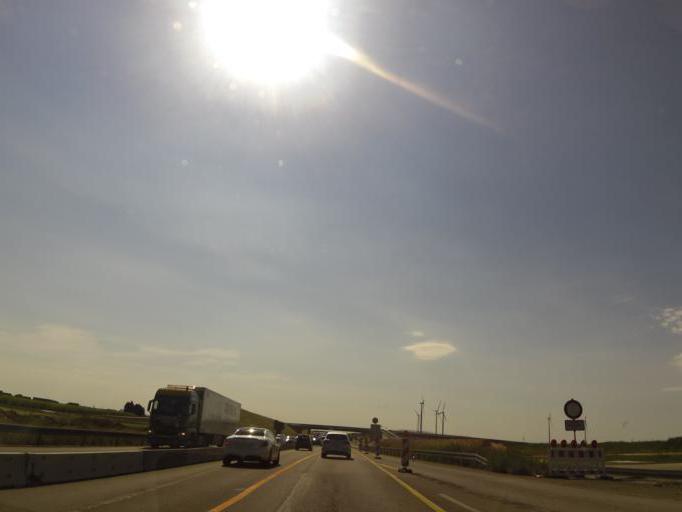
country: DE
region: Baden-Wuerttemberg
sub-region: Tuebingen Region
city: Nellingen
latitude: 48.4883
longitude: 9.8552
